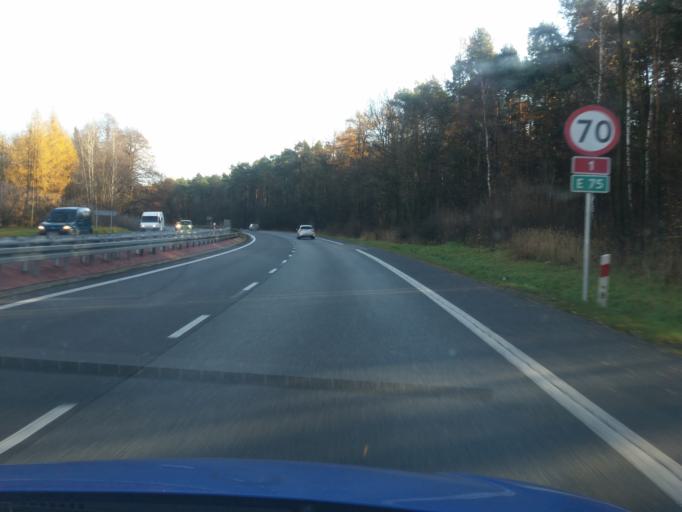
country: PL
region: Silesian Voivodeship
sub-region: Powiat myszkowski
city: Kozieglowy
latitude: 50.5407
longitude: 19.1812
